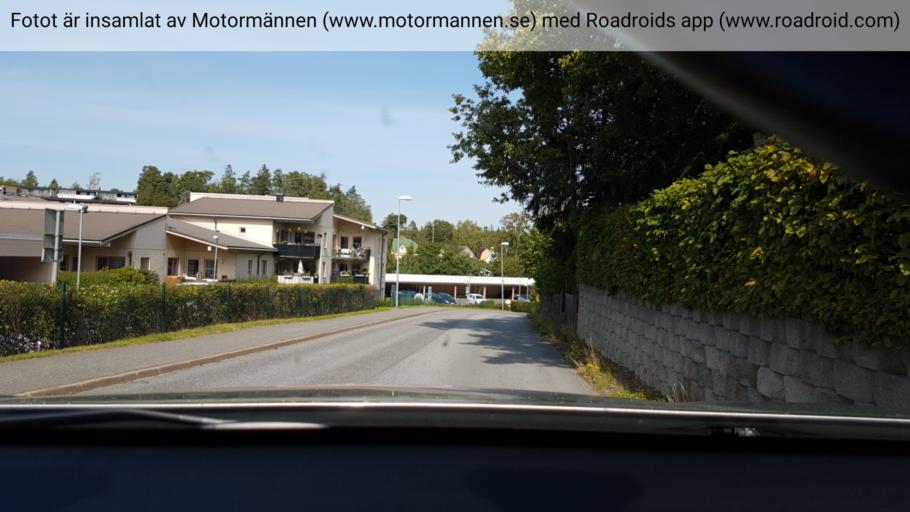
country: SE
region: Stockholm
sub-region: Huddinge Kommun
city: Huddinge
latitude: 59.2374
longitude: 17.9713
